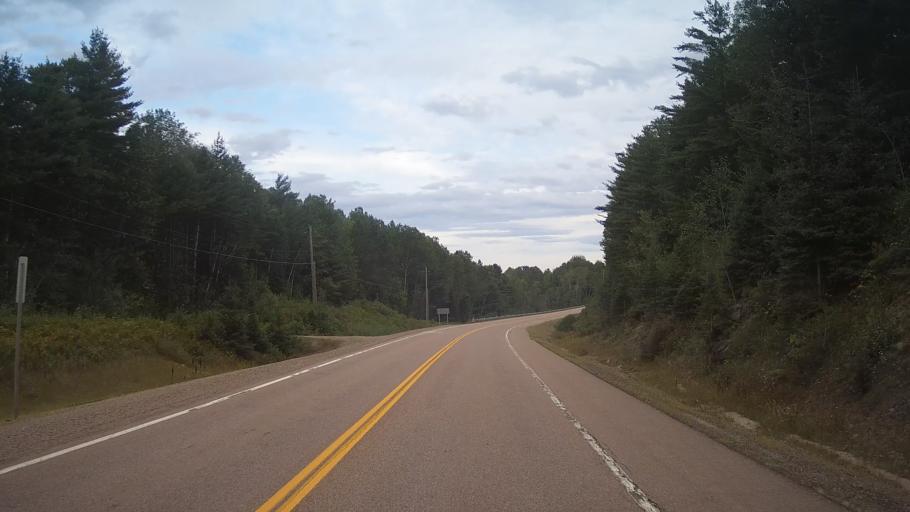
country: CA
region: Ontario
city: Deep River
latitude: 46.2105
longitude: -77.8895
